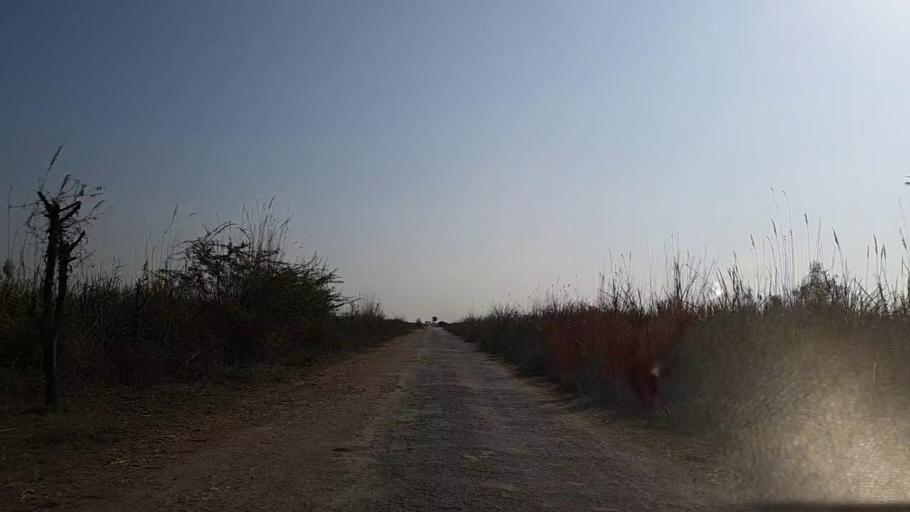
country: PK
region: Sindh
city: Tando Mittha Khan
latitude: 25.8879
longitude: 69.0768
